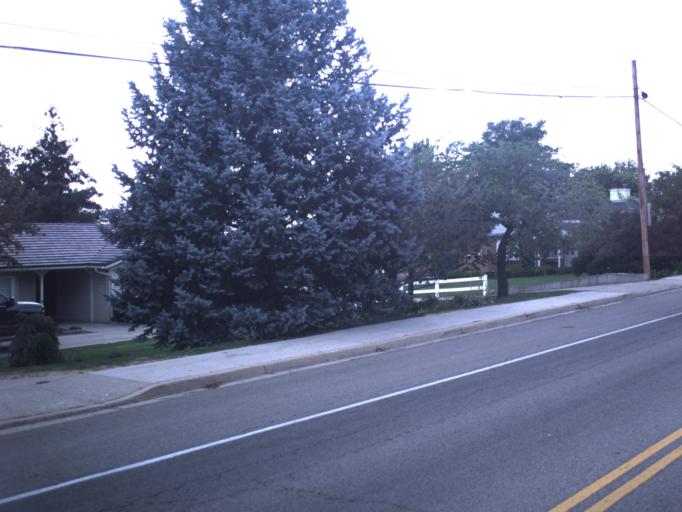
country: US
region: Utah
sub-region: Davis County
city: Centerville
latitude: 40.9465
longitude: -111.8815
